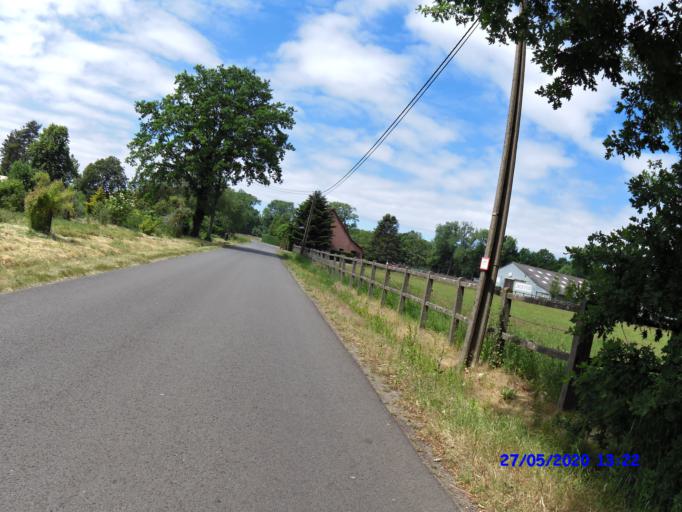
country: BE
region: Flanders
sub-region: Provincie Antwerpen
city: Geel
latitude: 51.2017
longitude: 4.9971
